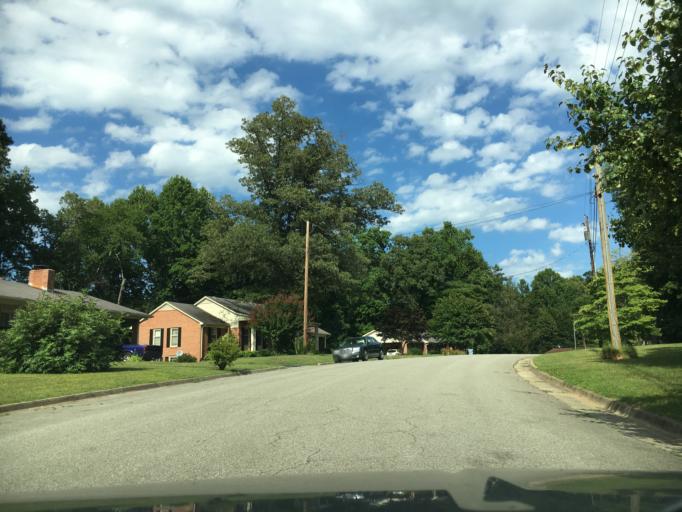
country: US
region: Virginia
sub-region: Halifax County
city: South Boston
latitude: 36.7123
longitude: -78.9093
